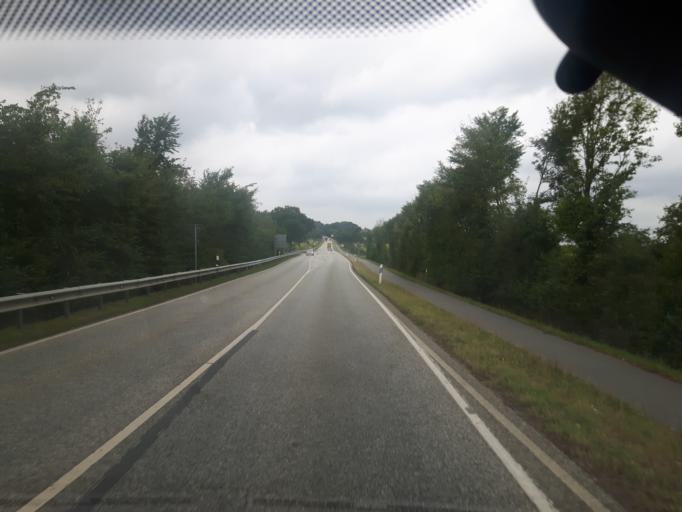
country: DE
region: Schleswig-Holstein
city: Borgstedt
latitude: 54.3492
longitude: 9.7014
